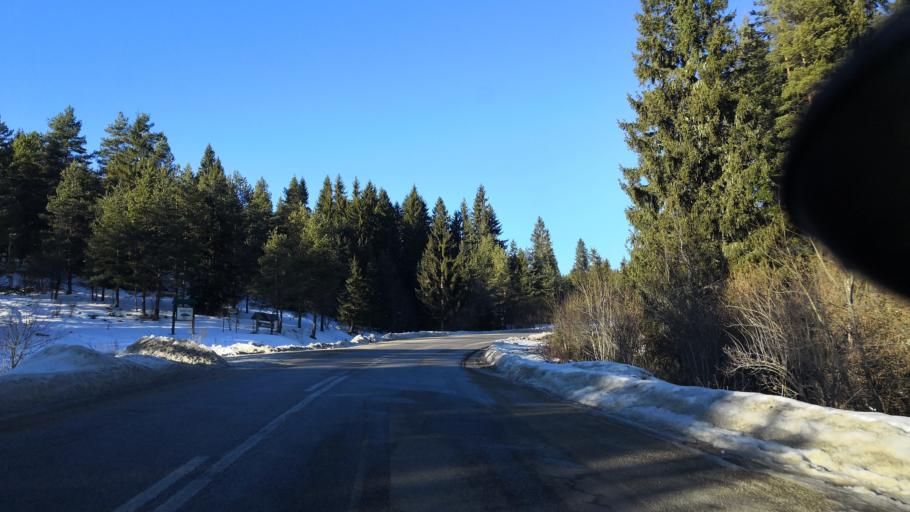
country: BA
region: Republika Srpska
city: Han Pijesak
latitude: 44.0233
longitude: 18.8818
